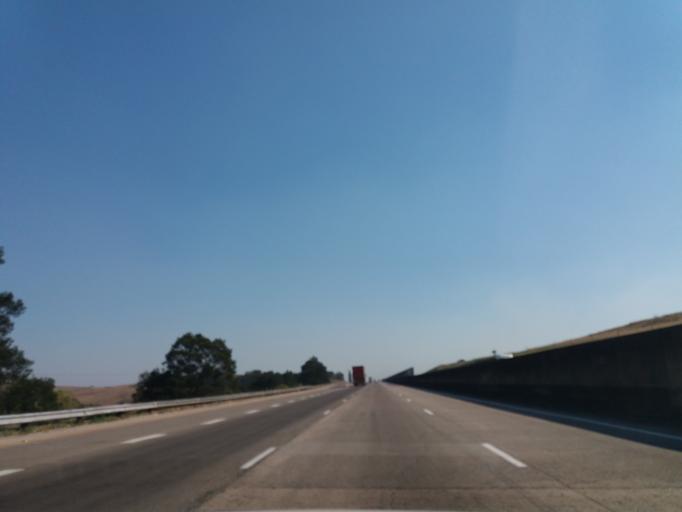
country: ZA
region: KwaZulu-Natal
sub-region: eThekwini Metropolitan Municipality
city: Mpumalanga
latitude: -29.7382
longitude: 30.6408
